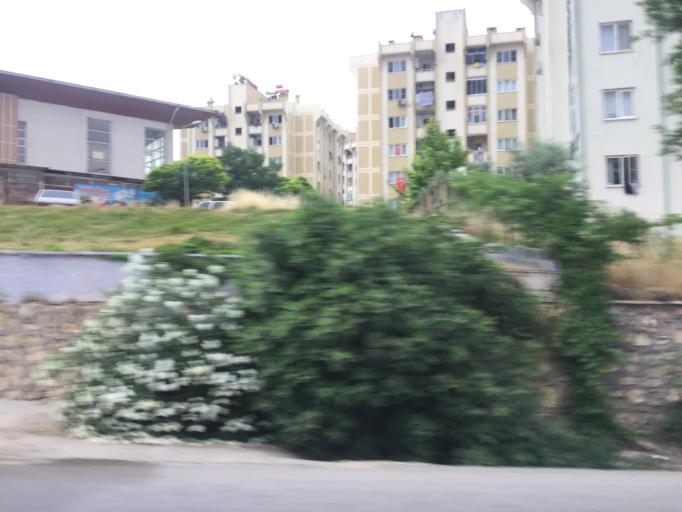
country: TR
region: Gaziantep
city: Gaziantep
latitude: 37.0499
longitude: 37.4216
